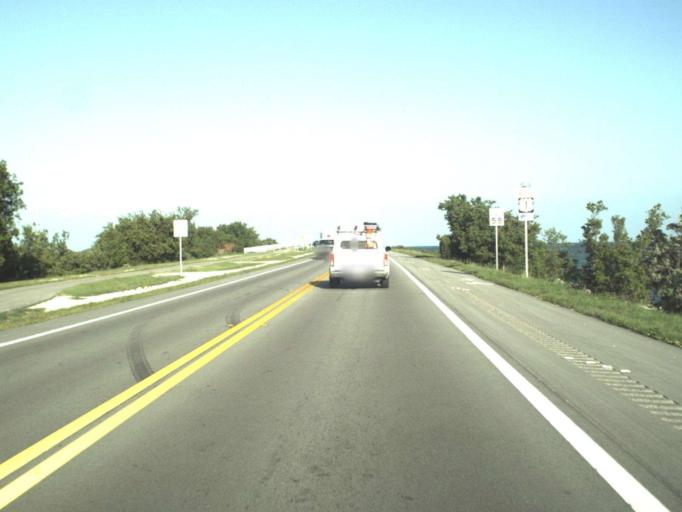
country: US
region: Florida
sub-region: Monroe County
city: Islamorada
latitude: 24.8404
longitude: -80.7840
